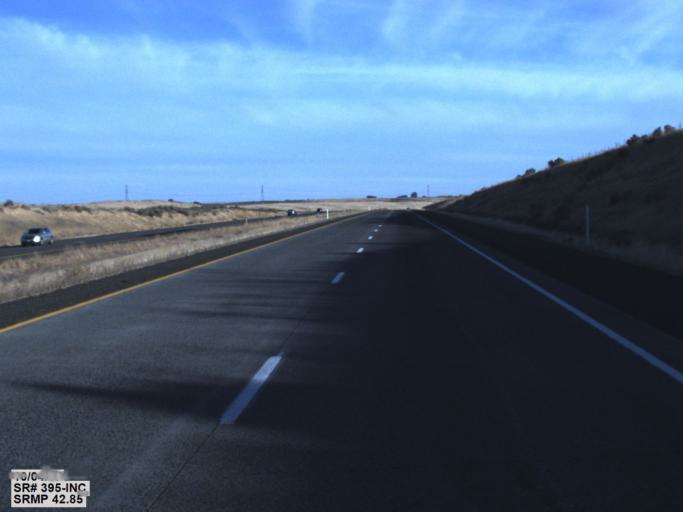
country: US
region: Washington
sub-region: Franklin County
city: Basin City
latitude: 46.5264
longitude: -119.0146
